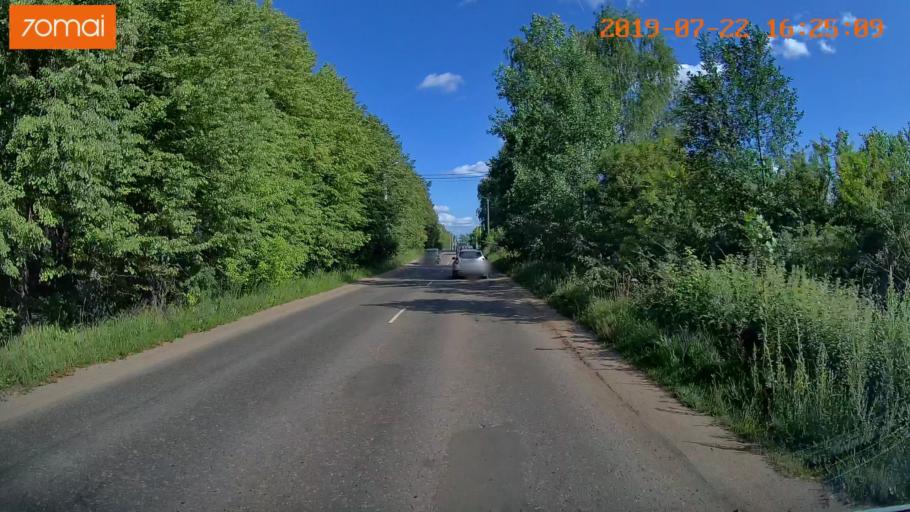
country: RU
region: Ivanovo
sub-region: Gorod Ivanovo
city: Ivanovo
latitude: 57.0550
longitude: 40.9224
